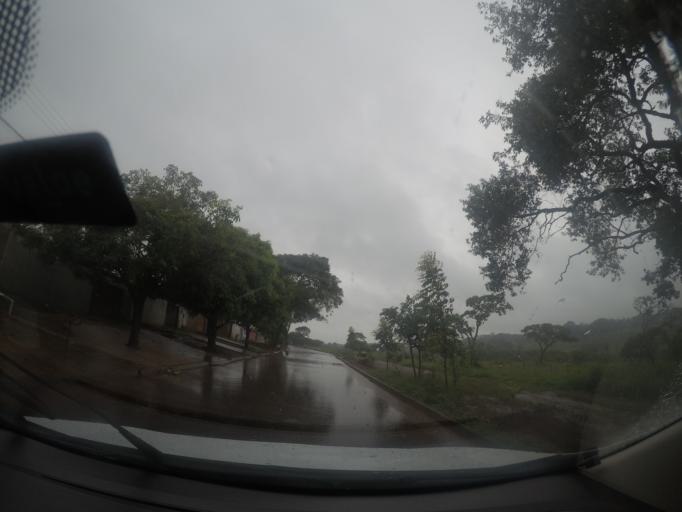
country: BR
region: Goias
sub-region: Goiania
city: Goiania
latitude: -16.5993
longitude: -49.3516
